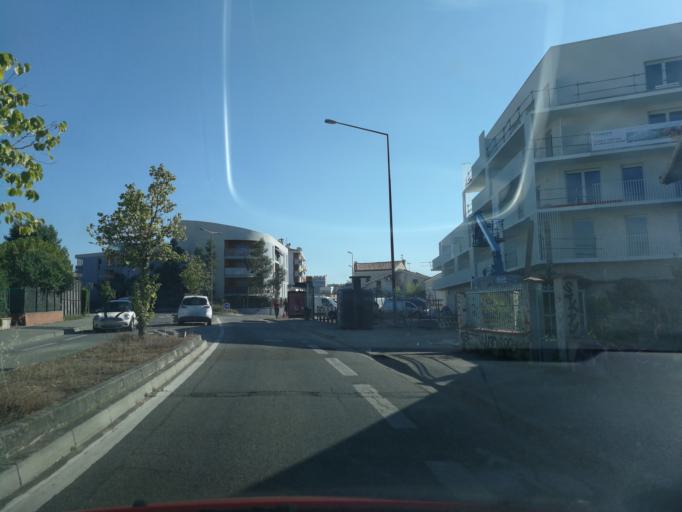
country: FR
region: Midi-Pyrenees
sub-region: Departement de la Haute-Garonne
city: Toulouse
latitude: 43.6238
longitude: 1.4543
